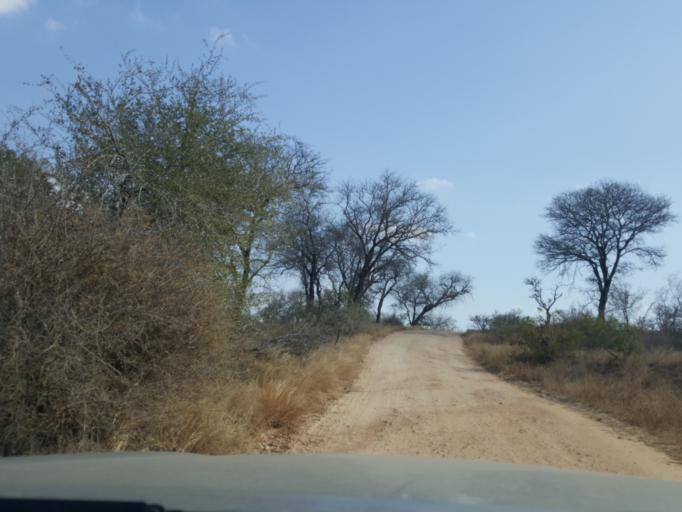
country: ZA
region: Mpumalanga
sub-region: Ehlanzeni District
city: Komatipoort
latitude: -25.2825
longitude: 31.7724
